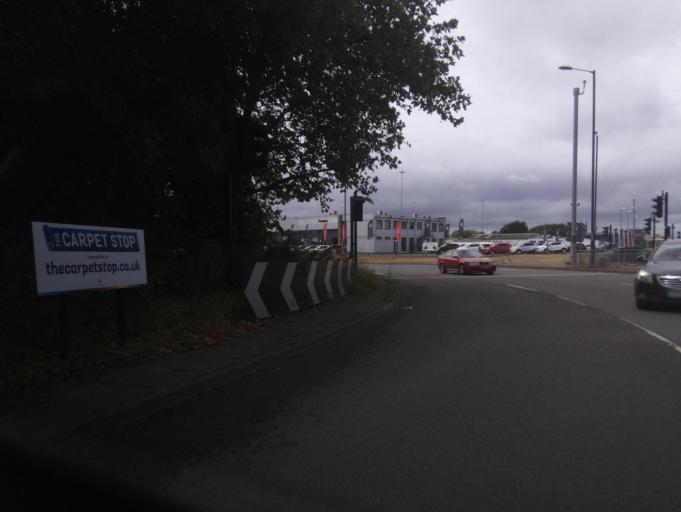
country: GB
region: England
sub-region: Derby
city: Derby
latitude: 52.9257
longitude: -1.4619
